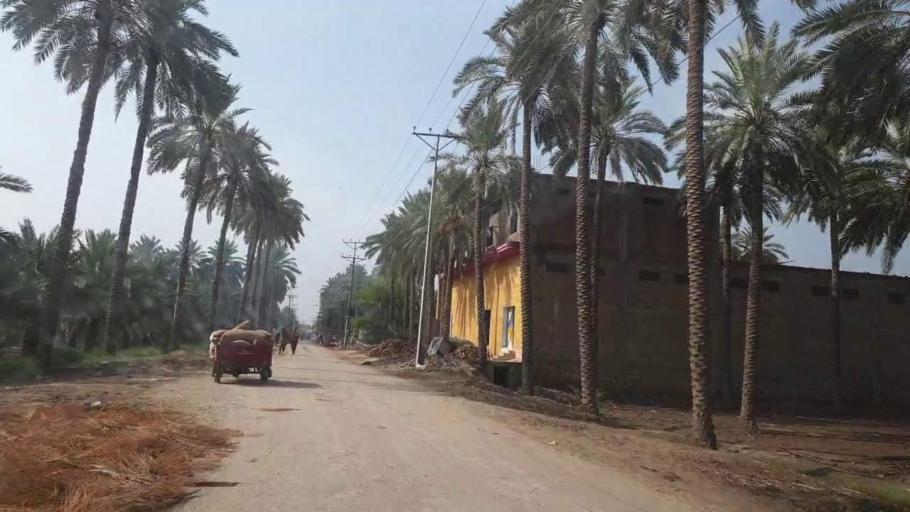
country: PK
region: Sindh
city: Khairpur
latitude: 27.5945
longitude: 68.7780
